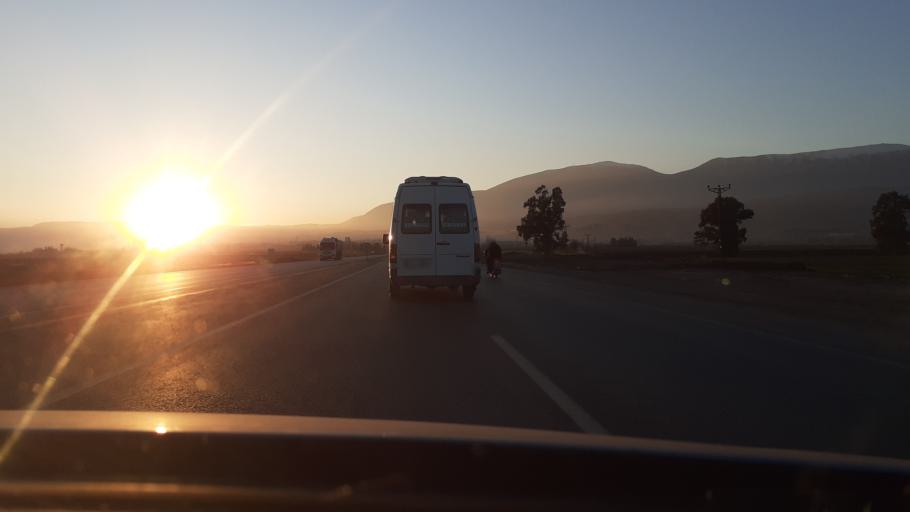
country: TR
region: Hatay
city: Kirikhan
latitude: 36.5047
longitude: 36.4091
